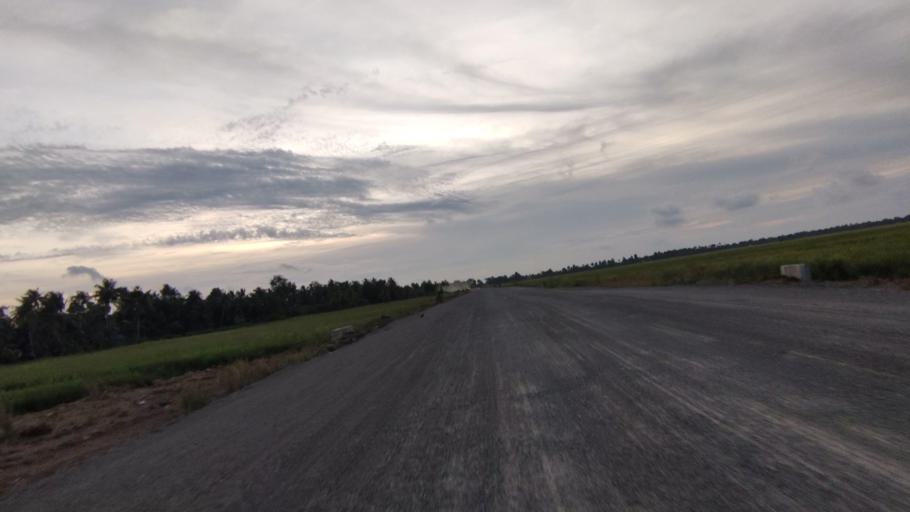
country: IN
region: Kerala
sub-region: Kottayam
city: Kottayam
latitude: 9.6472
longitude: 76.4733
